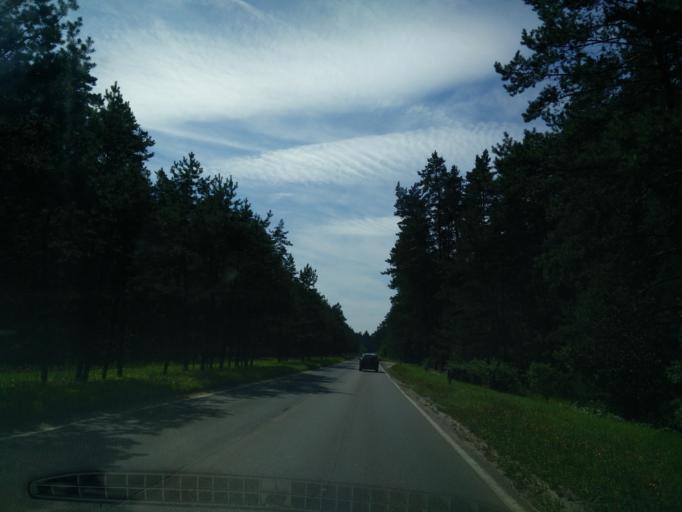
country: LT
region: Vilnius County
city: Rasos
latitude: 54.7520
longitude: 25.3622
